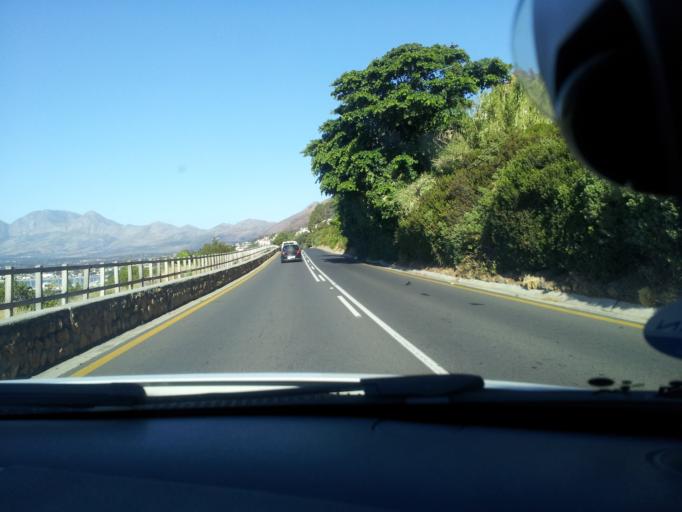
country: ZA
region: Western Cape
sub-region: Overberg District Municipality
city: Grabouw
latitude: -34.1685
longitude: 18.8517
